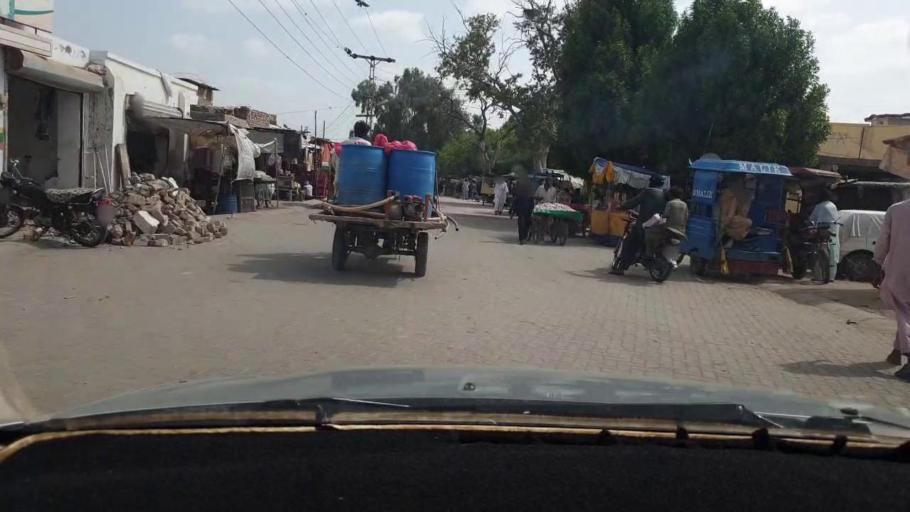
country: PK
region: Sindh
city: Digri
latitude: 25.0699
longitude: 69.2166
